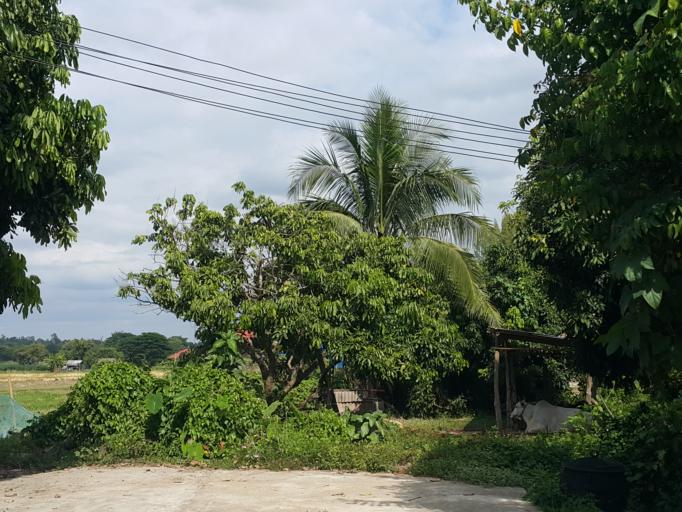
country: TH
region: Lampang
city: Chae Hom
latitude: 18.5631
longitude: 99.4482
